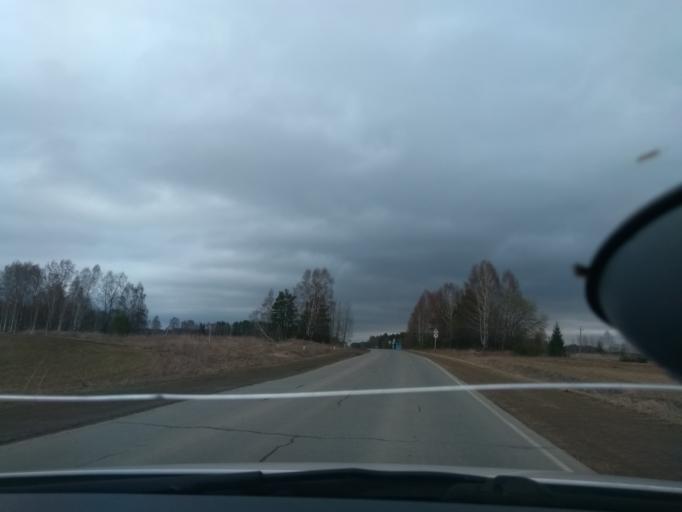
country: RU
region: Perm
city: Orda
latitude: 57.3409
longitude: 56.7824
